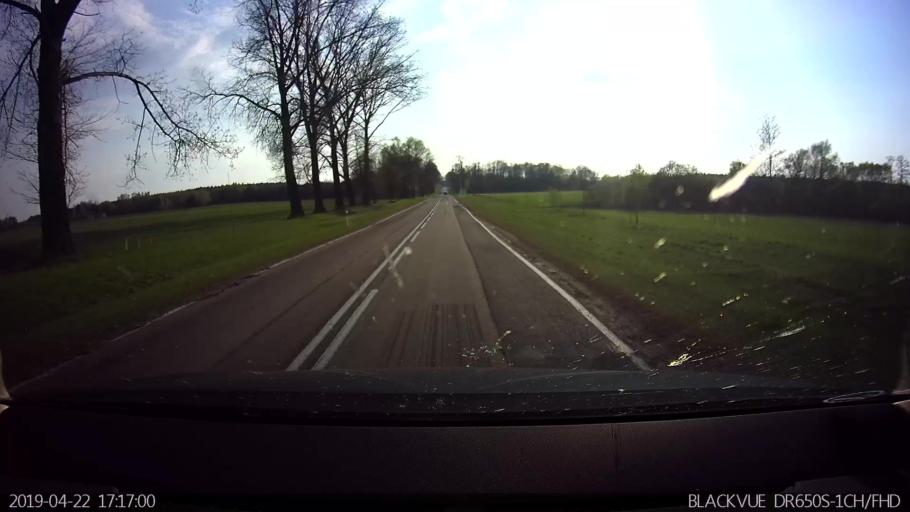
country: PL
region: Masovian Voivodeship
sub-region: Powiat sokolowski
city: Repki
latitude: 52.3904
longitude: 22.4477
